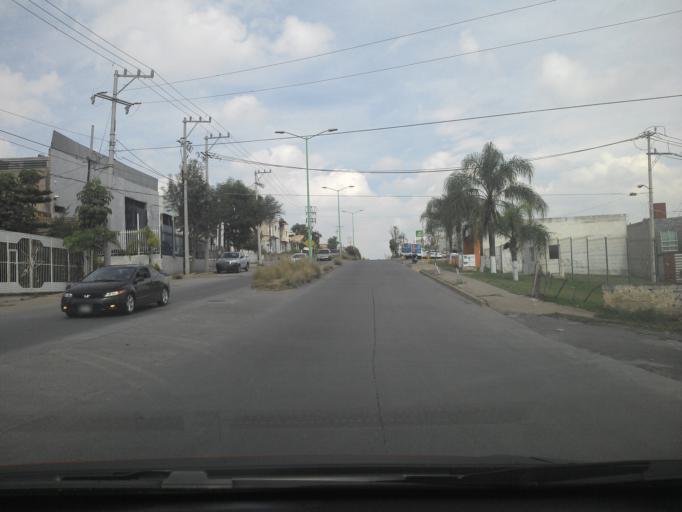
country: MX
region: Jalisco
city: Las Pintas de Arriba
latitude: 20.5917
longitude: -103.3491
